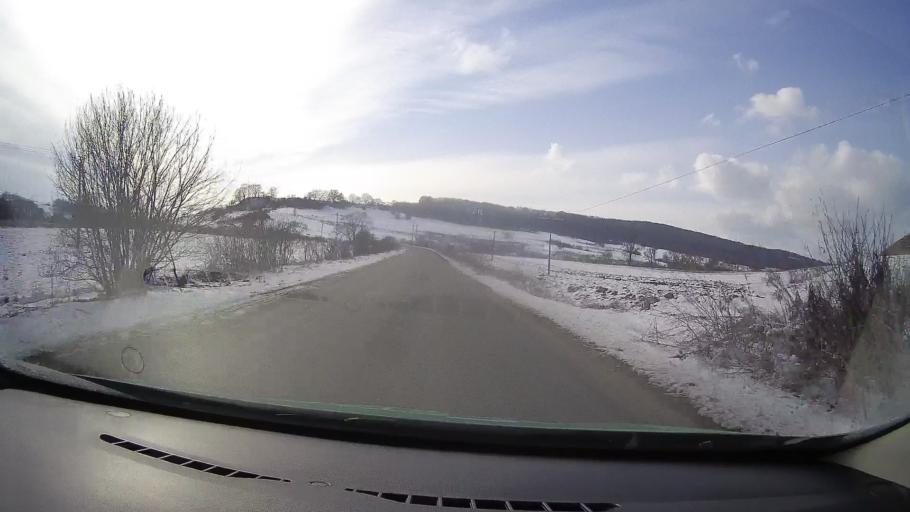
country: RO
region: Sibiu
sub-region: Comuna Iacobeni
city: Iacobeni
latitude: 46.0207
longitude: 24.7000
